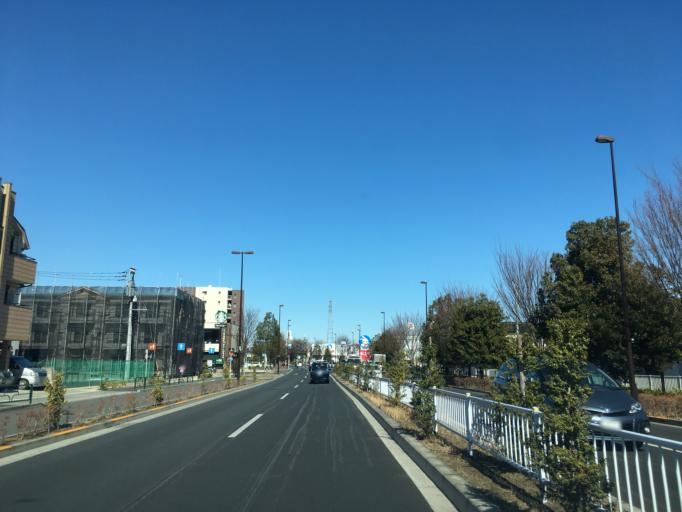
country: JP
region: Tokyo
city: Mitaka-shi
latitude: 35.6878
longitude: 139.5503
